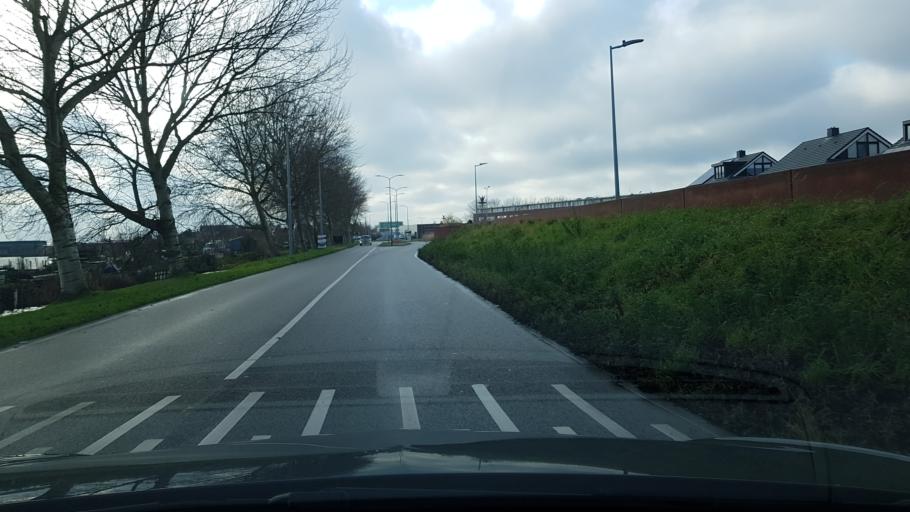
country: NL
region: South Holland
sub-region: Gemeente Lisse
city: Lisse
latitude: 52.2554
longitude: 4.5807
